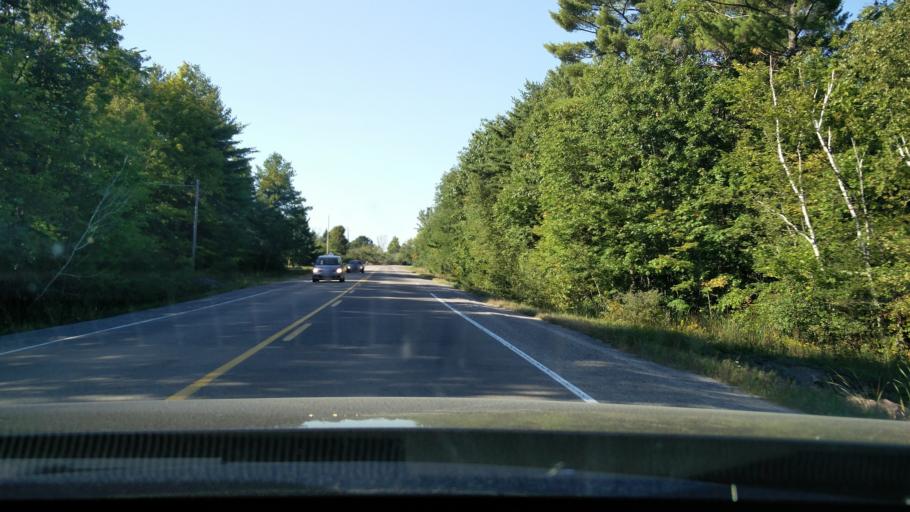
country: CA
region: Ontario
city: Perth
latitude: 44.6912
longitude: -76.3995
